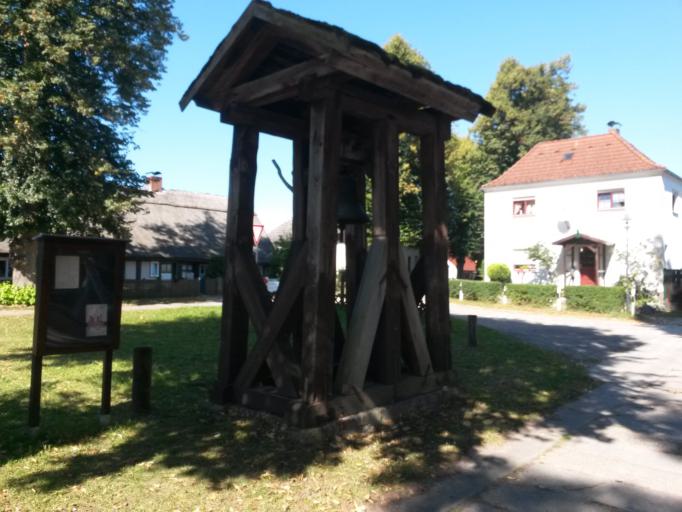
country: DE
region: Brandenburg
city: Lychen
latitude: 53.1338
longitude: 13.3768
